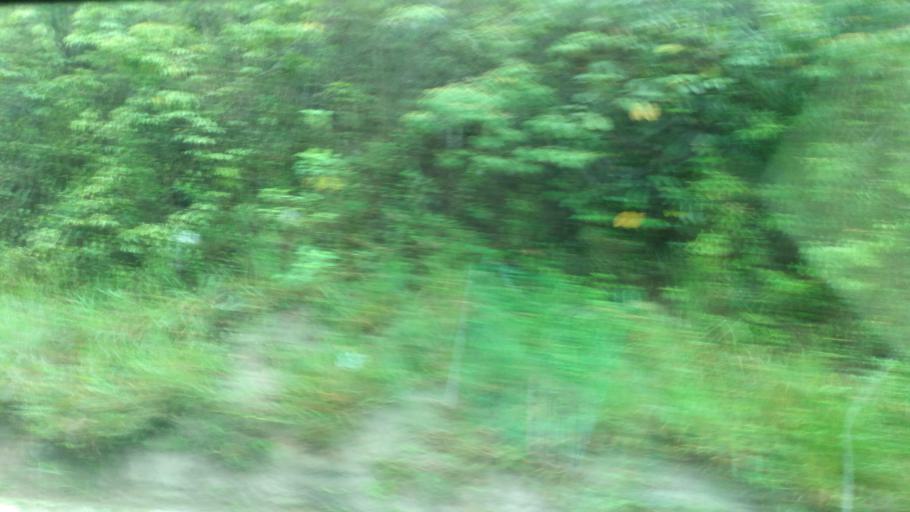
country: BR
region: Pernambuco
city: Garanhuns
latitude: -8.8780
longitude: -36.5120
